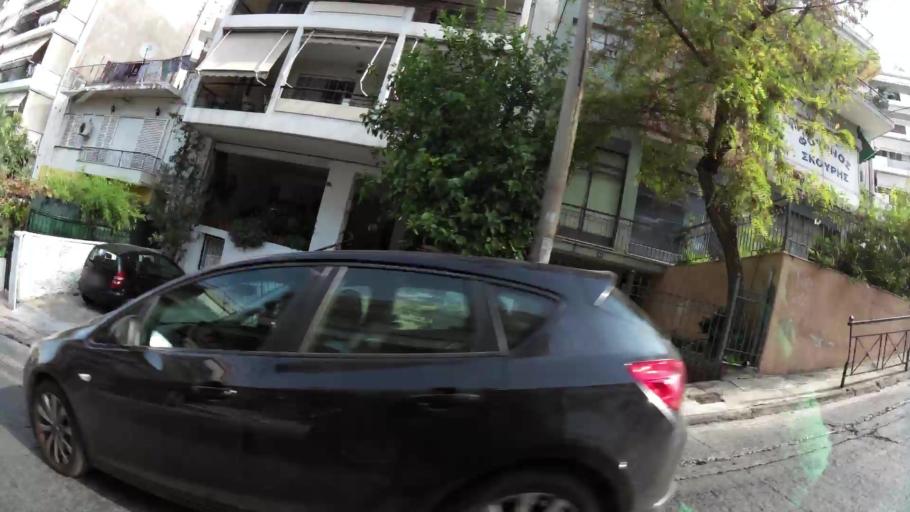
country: GR
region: Attica
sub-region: Nomarchia Athinas
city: Galatsi
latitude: 38.0092
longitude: 23.7495
